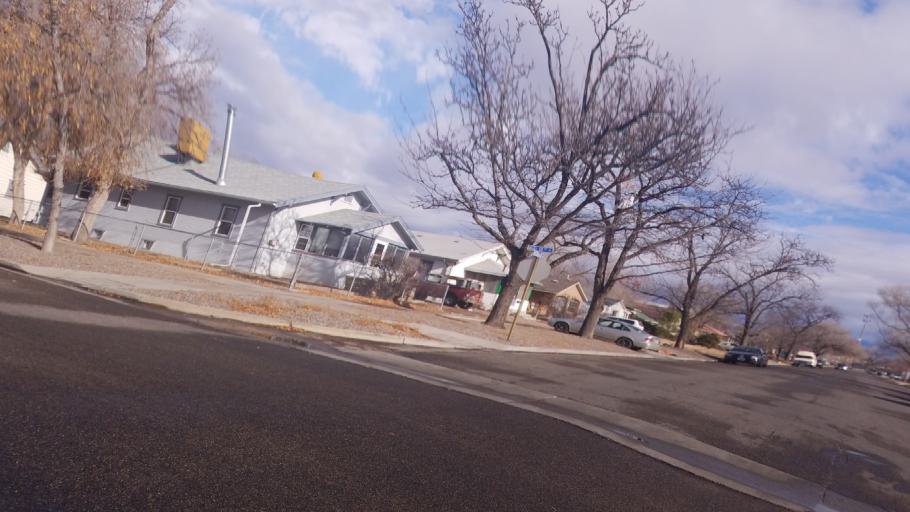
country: US
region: Colorado
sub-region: Mesa County
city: Grand Junction
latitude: 39.0664
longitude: -108.5509
